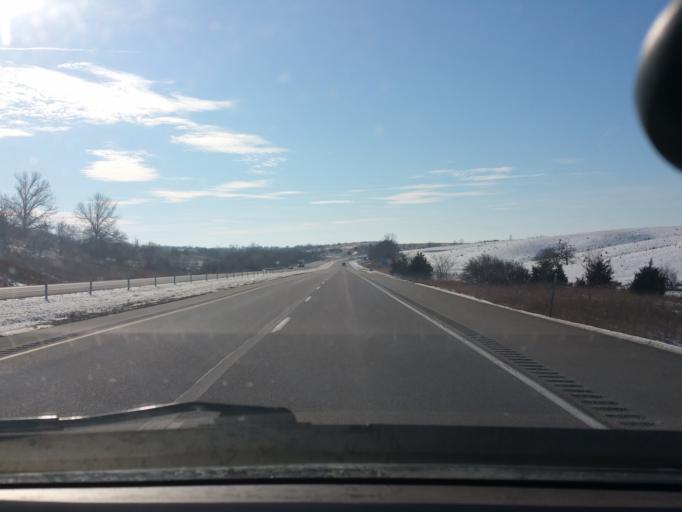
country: US
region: Iowa
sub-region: Clarke County
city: Osceola
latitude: 41.0613
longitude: -93.7817
